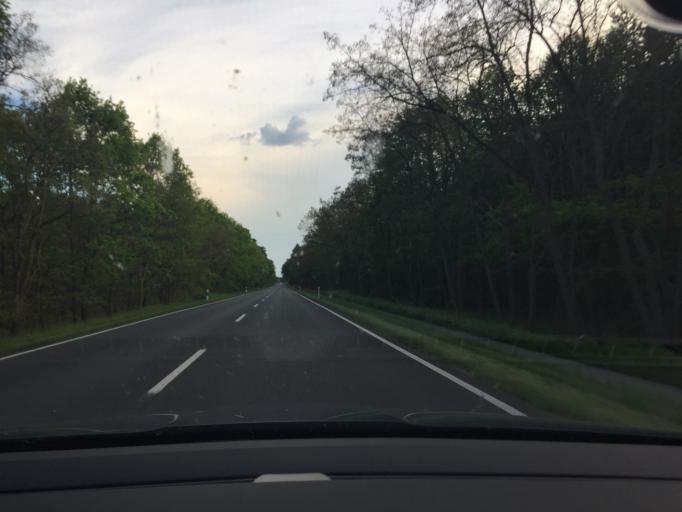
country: DE
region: Brandenburg
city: Treuenbrietzen
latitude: 52.1418
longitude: 12.9163
